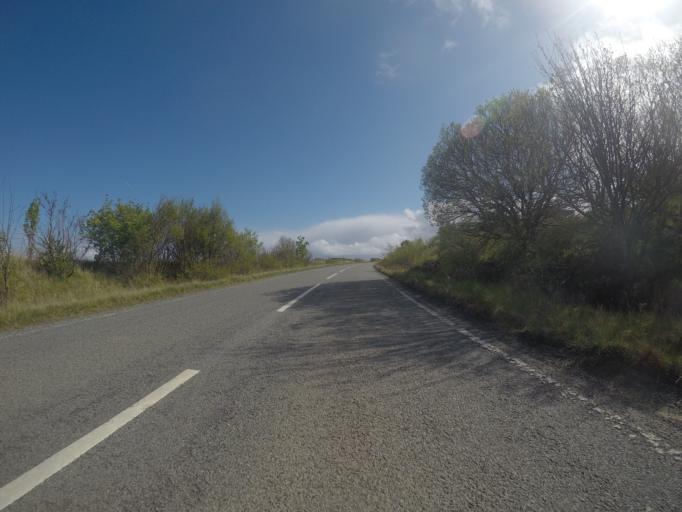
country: GB
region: Scotland
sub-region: Highland
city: Portree
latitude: 57.5909
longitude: -6.1587
